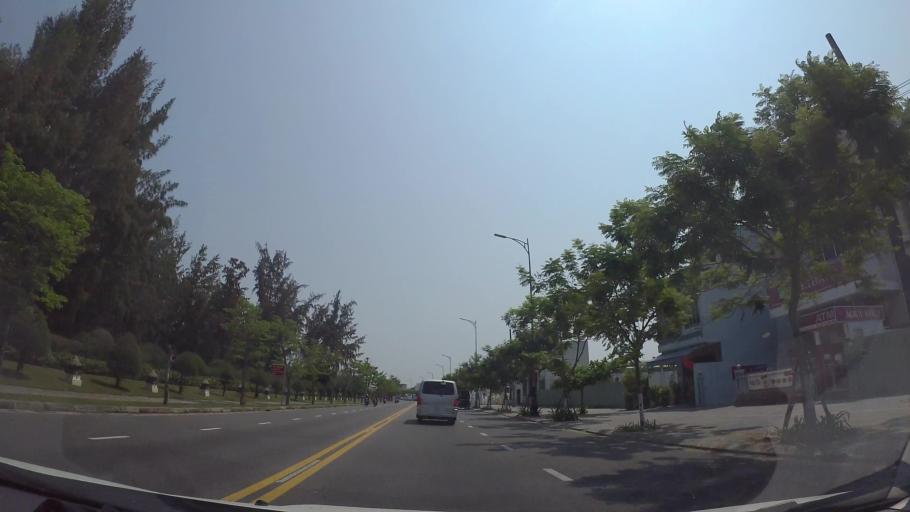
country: VN
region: Da Nang
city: Ngu Hanh Son
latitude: 15.9979
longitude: 108.2676
